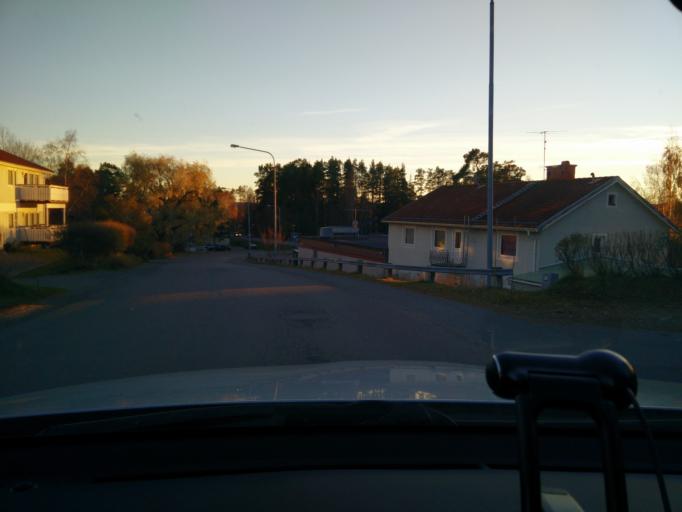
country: SE
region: Vaesternorrland
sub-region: Sundsvalls Kommun
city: Matfors
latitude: 62.3514
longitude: 17.0371
